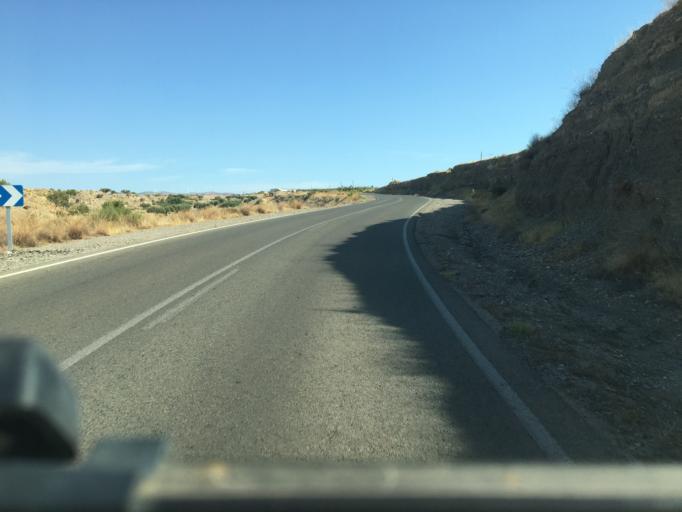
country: ES
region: Andalusia
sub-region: Provincia de Almeria
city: Huercal-Overa
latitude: 37.4333
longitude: -1.9742
